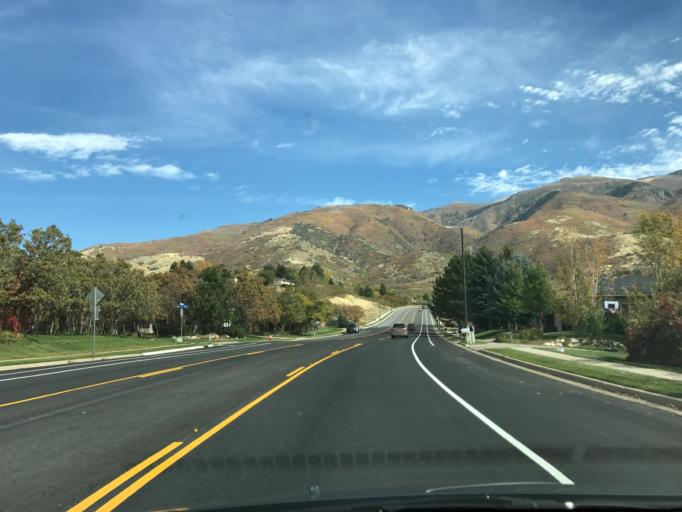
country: US
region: Utah
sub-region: Davis County
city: South Weber
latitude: 41.0911
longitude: -111.9172
